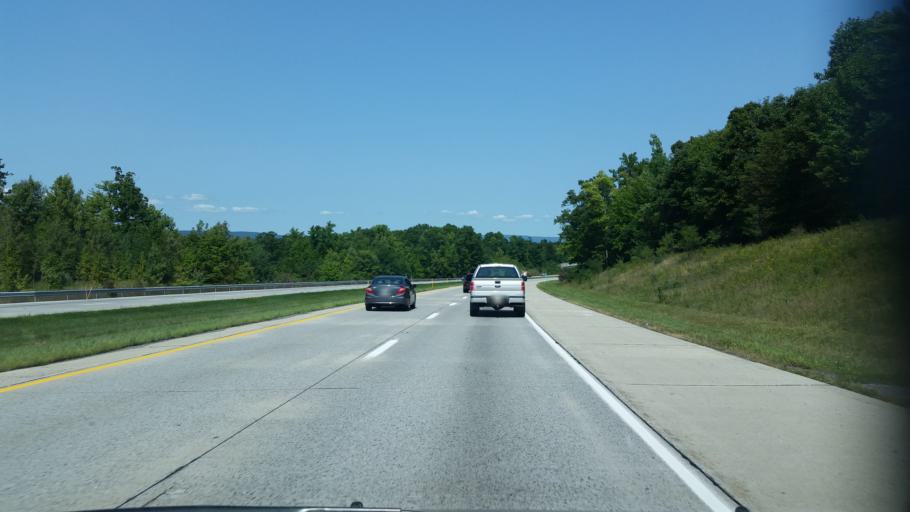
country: US
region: Pennsylvania
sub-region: Blair County
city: Greenwood
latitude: 40.5342
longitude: -78.3497
